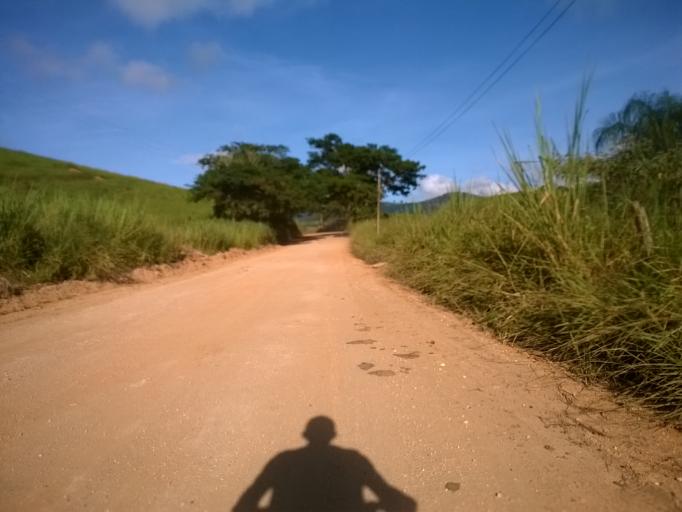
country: BR
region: Minas Gerais
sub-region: Uba
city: Uba
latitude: -21.0800
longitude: -42.9850
